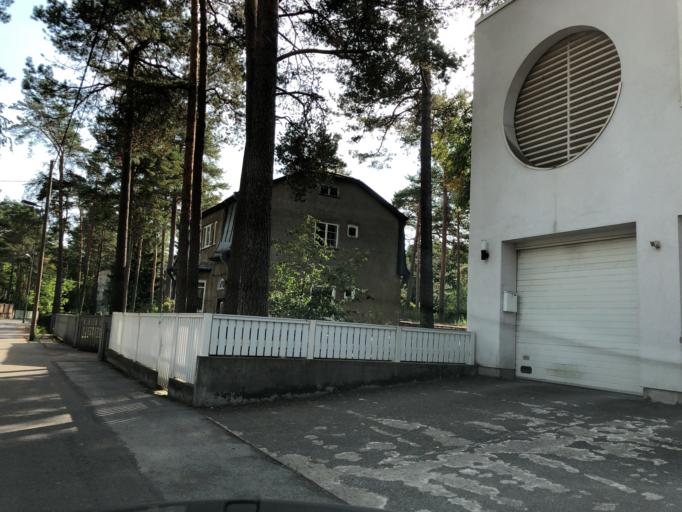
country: EE
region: Harju
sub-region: Tallinna linn
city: Tallinn
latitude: 59.3813
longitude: 24.6935
